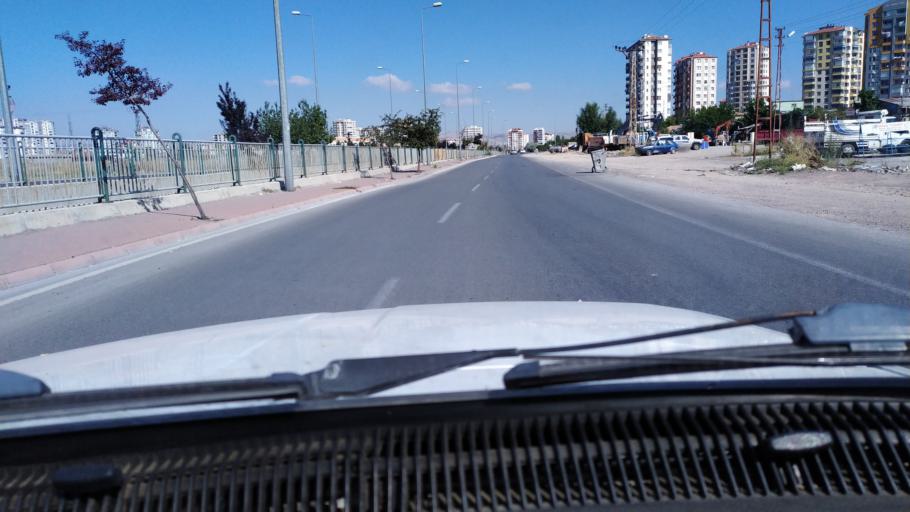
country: TR
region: Kayseri
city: Kocasinan
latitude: 38.7354
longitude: 35.5460
